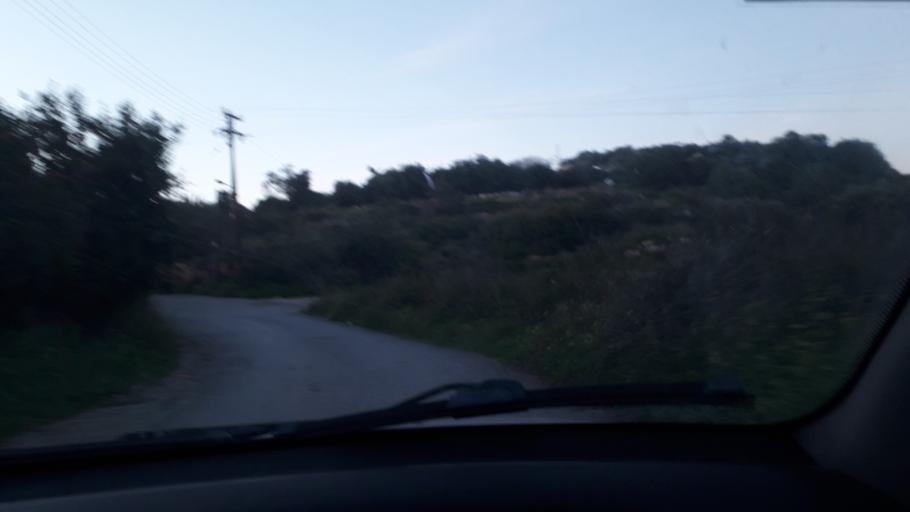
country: GR
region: Crete
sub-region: Nomos Rethymnis
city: Panormos
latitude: 35.3810
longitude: 24.6226
